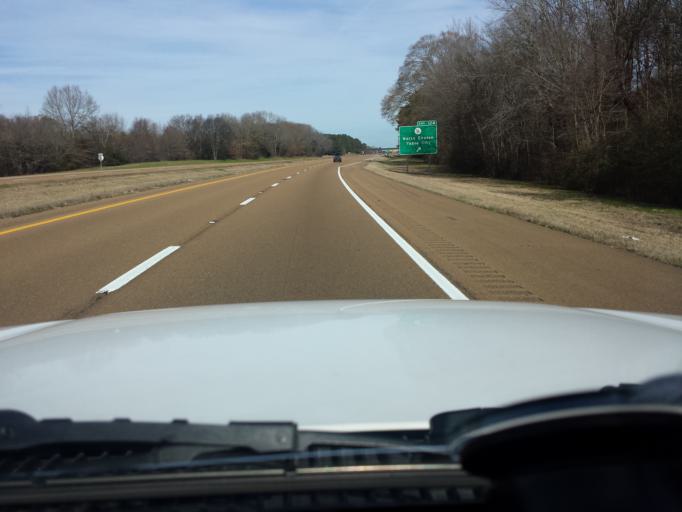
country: US
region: Mississippi
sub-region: Madison County
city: Canton
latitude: 32.6745
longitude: -90.0600
